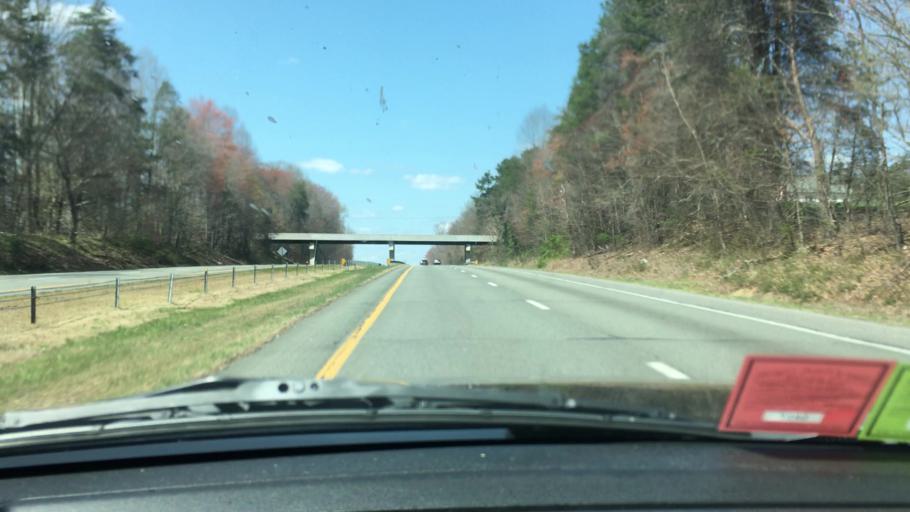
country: US
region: North Carolina
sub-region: Surry County
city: Pilot Mountain
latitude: 36.3869
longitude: -80.4897
